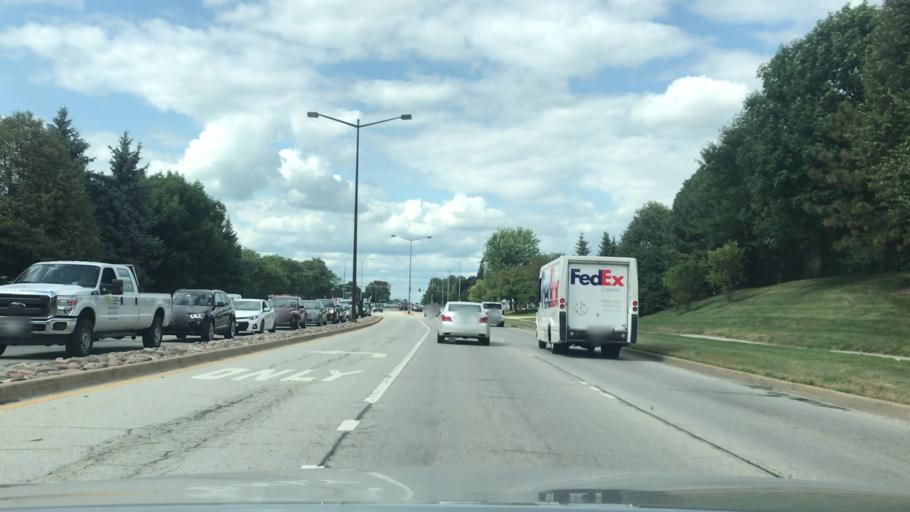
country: US
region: Illinois
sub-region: Kane County
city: Aurora
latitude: 41.7567
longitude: -88.2432
